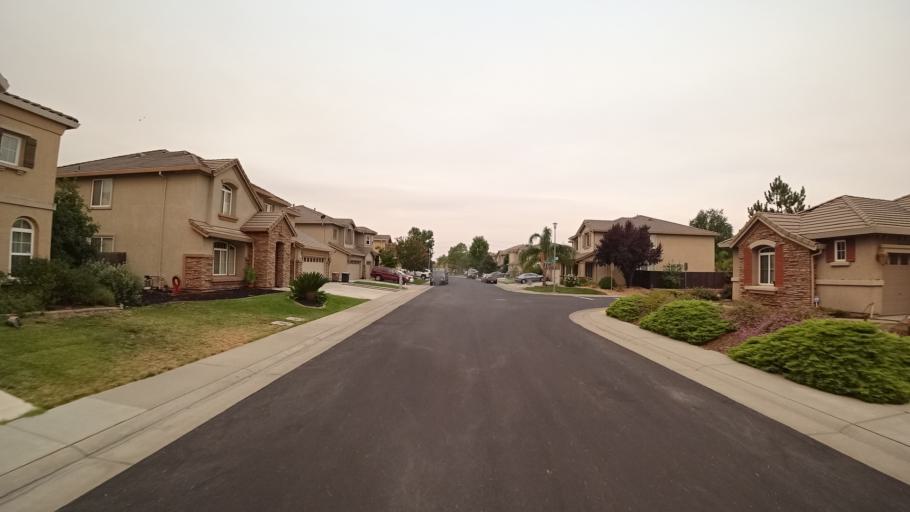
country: US
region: California
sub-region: Sacramento County
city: Laguna
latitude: 38.3826
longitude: -121.4467
